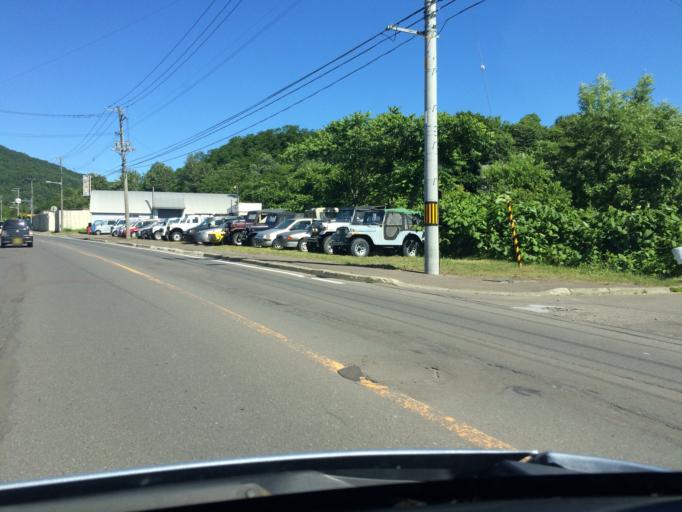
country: JP
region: Hokkaido
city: Sapporo
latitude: 43.0070
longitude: 141.3135
